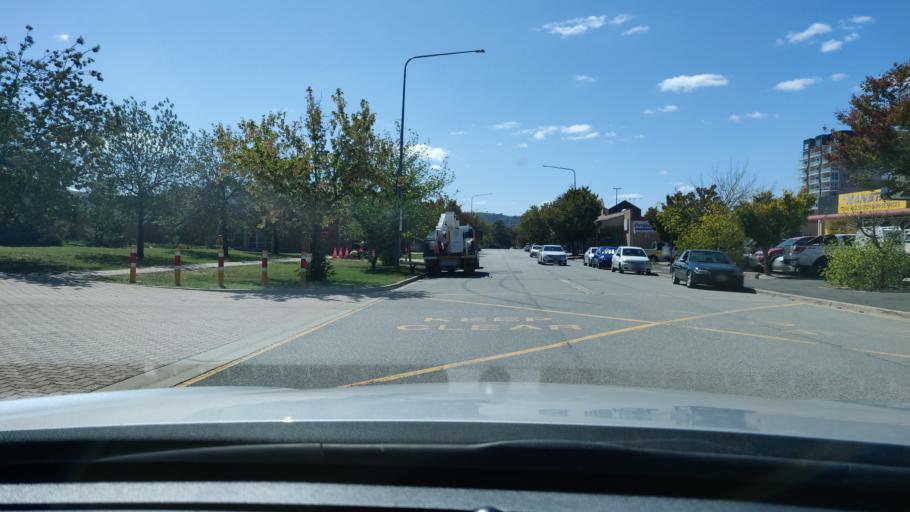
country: AU
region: Australian Capital Territory
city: Macarthur
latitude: -35.4201
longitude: 149.0682
